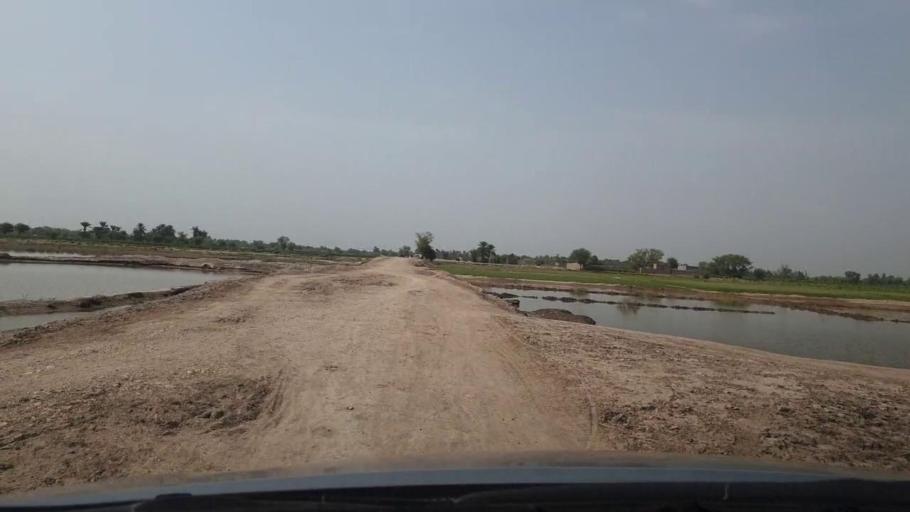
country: PK
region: Sindh
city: Rohri
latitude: 27.6670
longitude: 69.0136
